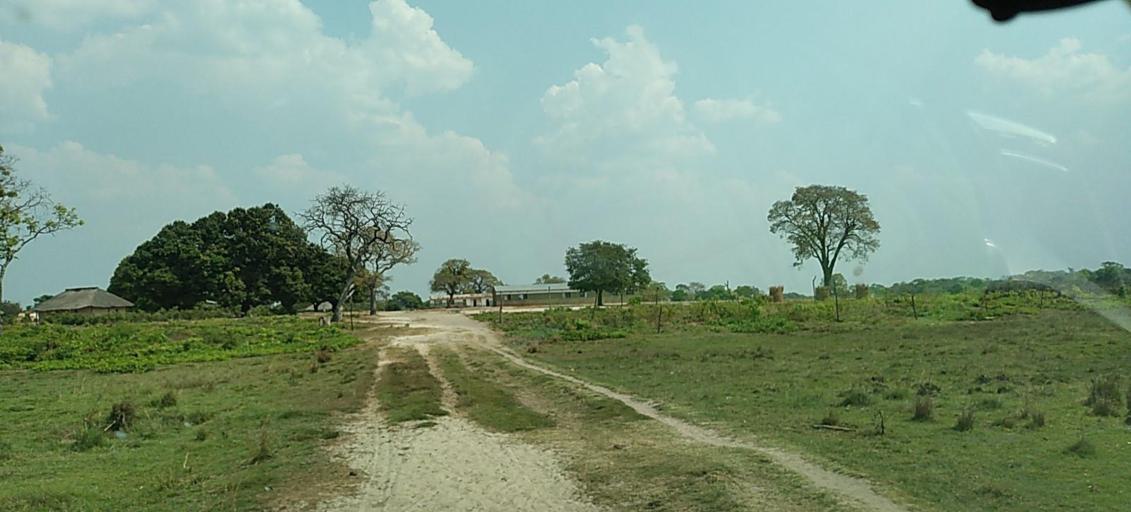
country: ZM
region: North-Western
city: Kabompo
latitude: -13.4483
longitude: 23.6674
